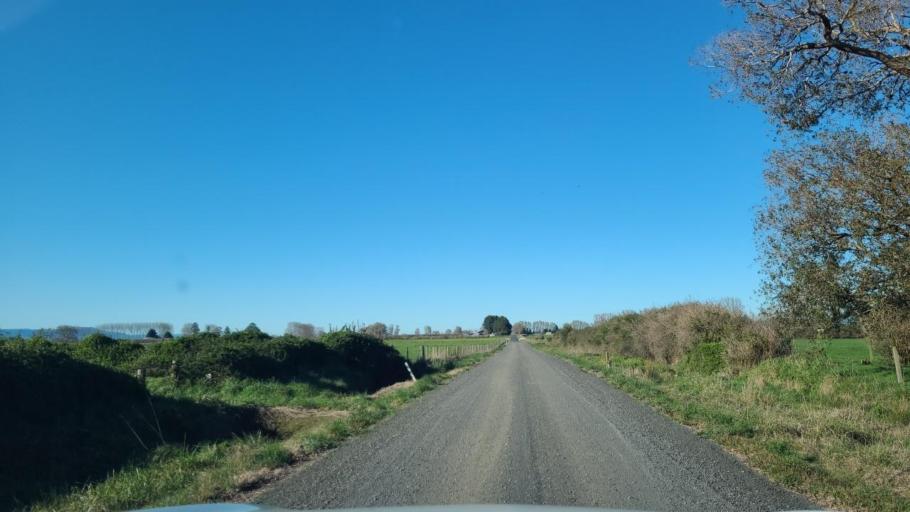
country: NZ
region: Bay of Plenty
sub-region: Western Bay of Plenty District
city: Katikati
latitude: -37.5908
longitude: 175.7131
